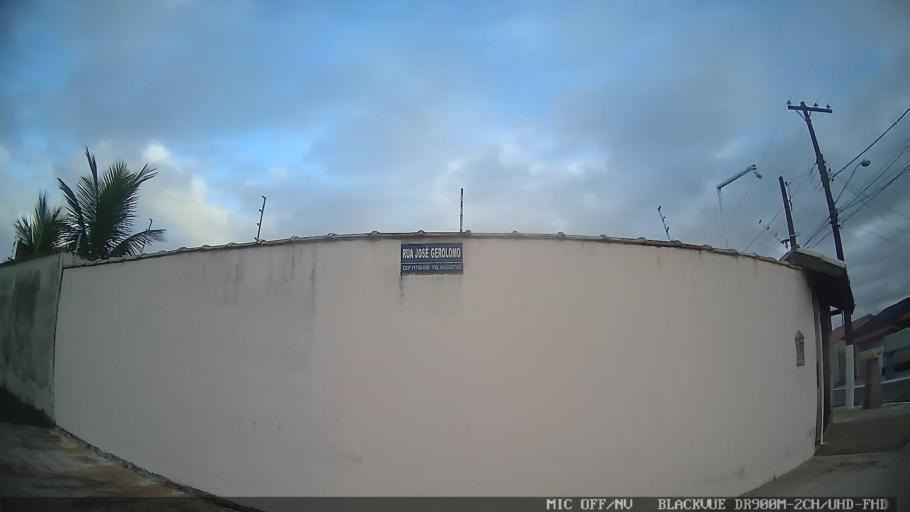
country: BR
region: Sao Paulo
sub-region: Itanhaem
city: Itanhaem
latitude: -24.2323
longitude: -46.8845
